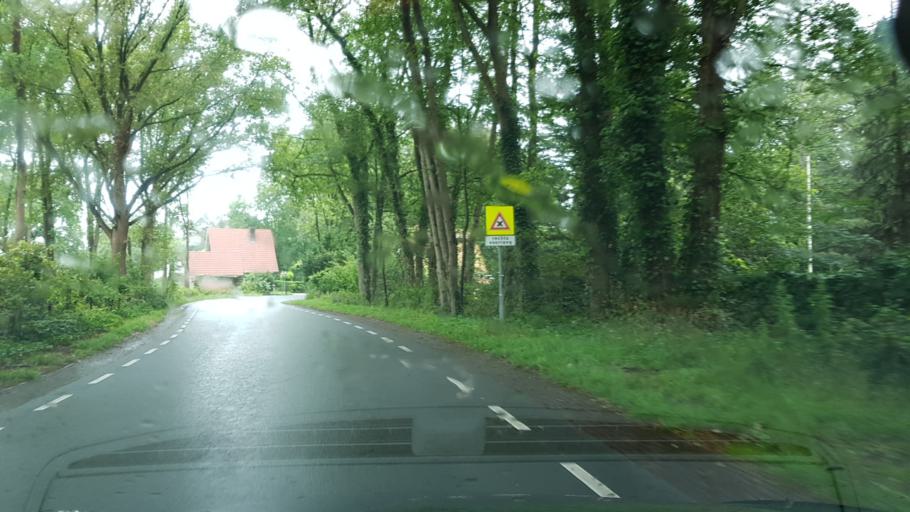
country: NL
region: Overijssel
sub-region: Gemeente Hof van Twente
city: Markelo
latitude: 52.2883
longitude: 6.4164
